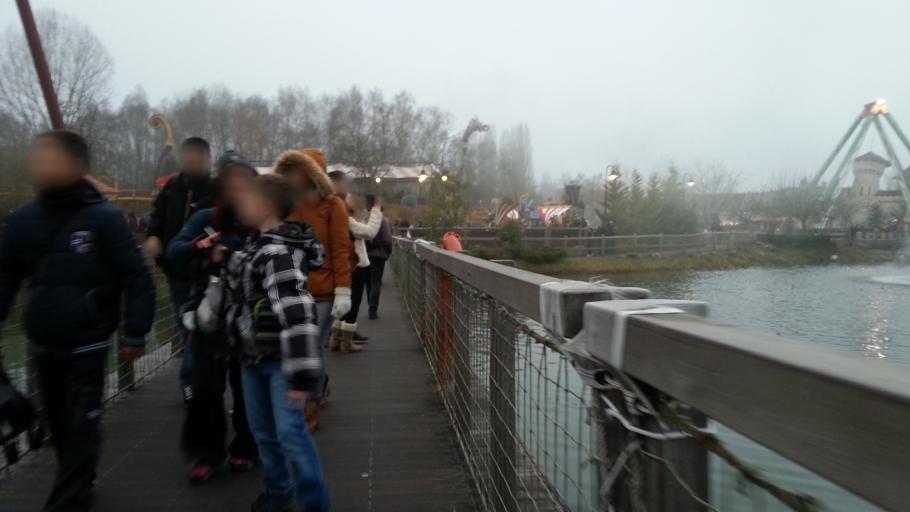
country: FR
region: Picardie
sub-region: Departement de l'Oise
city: Thiers-sur-Theve
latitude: 49.1319
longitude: 2.5719
